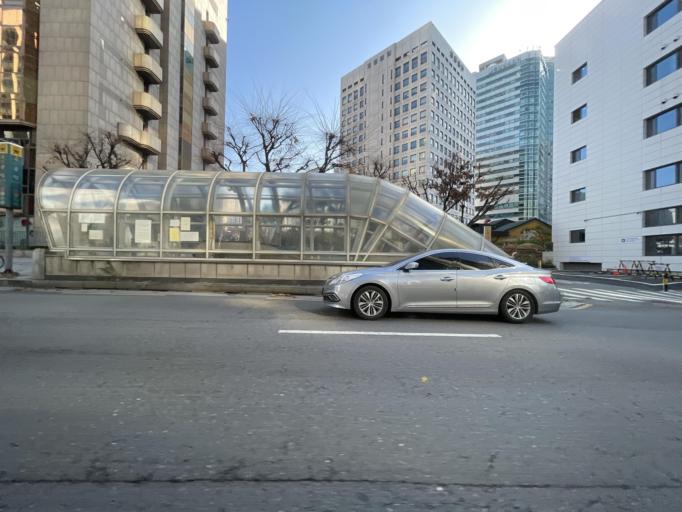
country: KR
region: Seoul
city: Seoul
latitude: 37.5452
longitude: 126.9520
